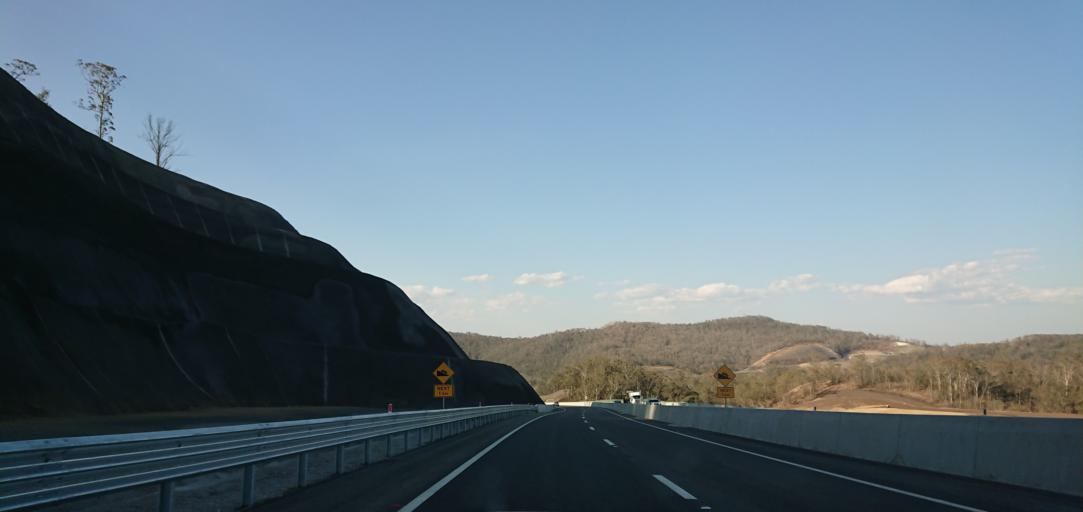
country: AU
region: Queensland
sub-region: Toowoomba
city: Wilsonton Heights
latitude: -27.5082
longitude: 151.9690
